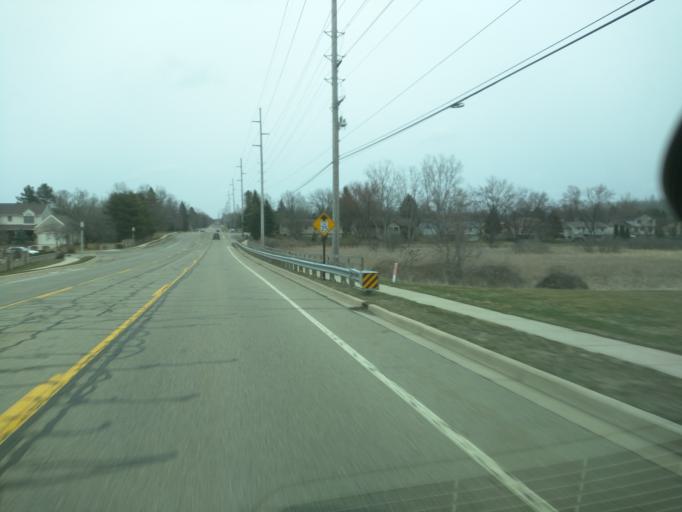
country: US
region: Michigan
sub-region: Eaton County
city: Waverly
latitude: 42.7555
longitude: -84.6320
